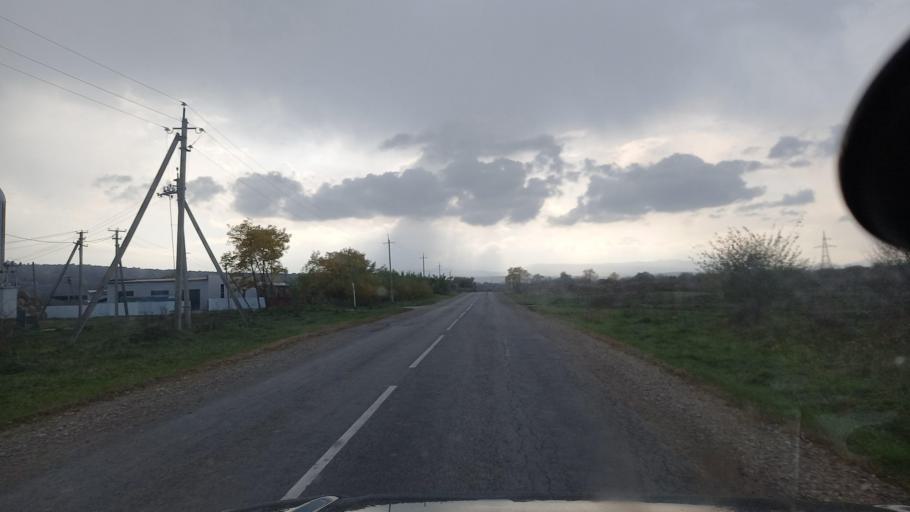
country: RU
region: Krasnodarskiy
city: Gubskaya
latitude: 44.3536
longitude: 40.6996
